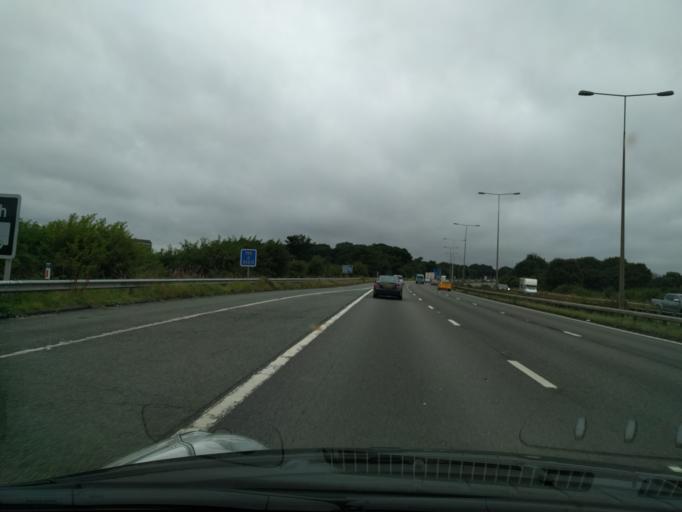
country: GB
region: England
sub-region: Borough of Wigan
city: Ashton in Makerfield
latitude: 53.4656
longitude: -2.6264
